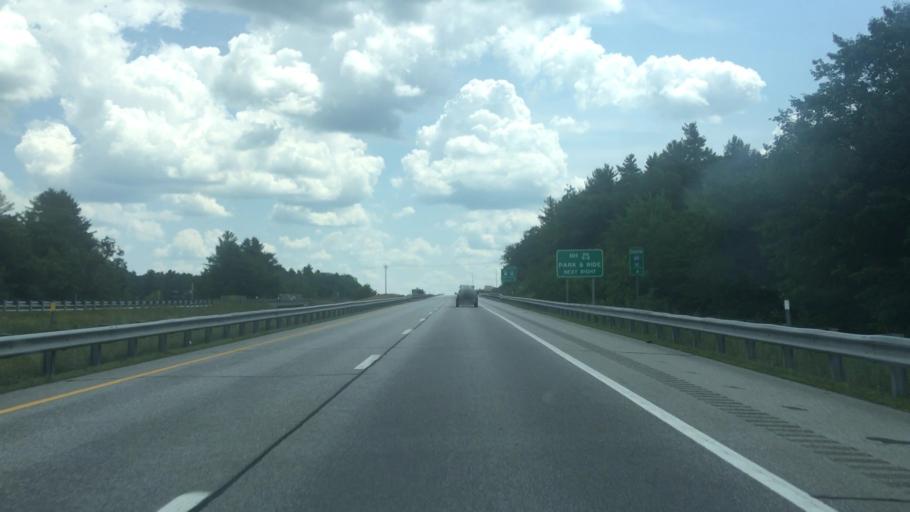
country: US
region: New Hampshire
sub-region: Merrimack County
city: New London
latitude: 43.4293
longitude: -72.0407
